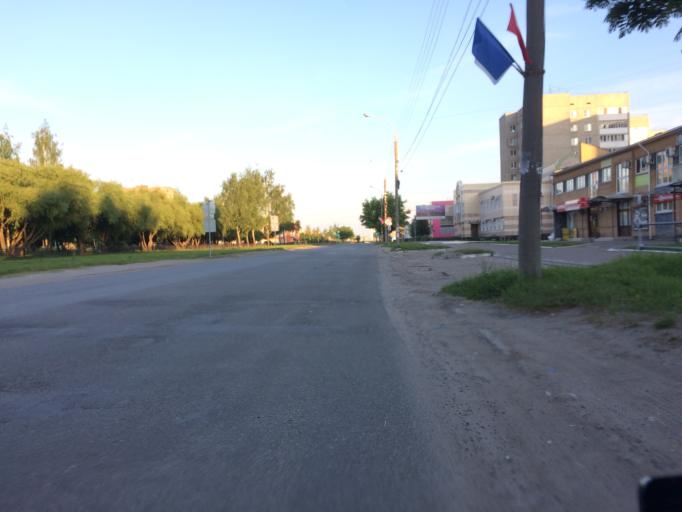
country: RU
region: Mariy-El
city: Medvedevo
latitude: 56.6414
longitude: 47.8388
